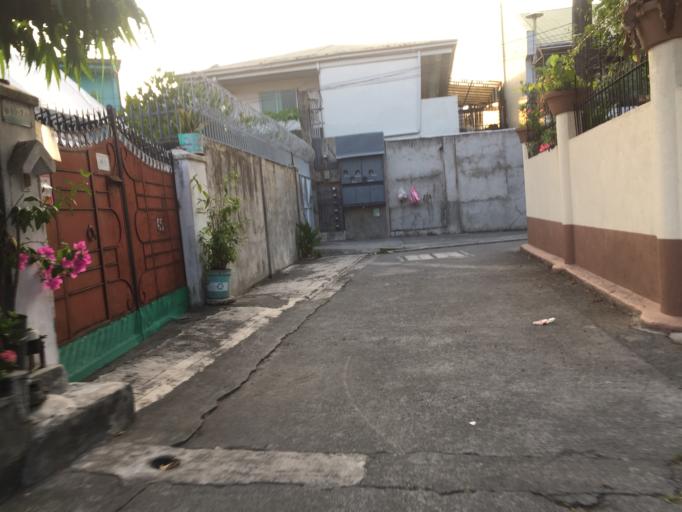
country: PH
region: Calabarzon
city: Bagong Pagasa
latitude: 14.6764
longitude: 121.0237
